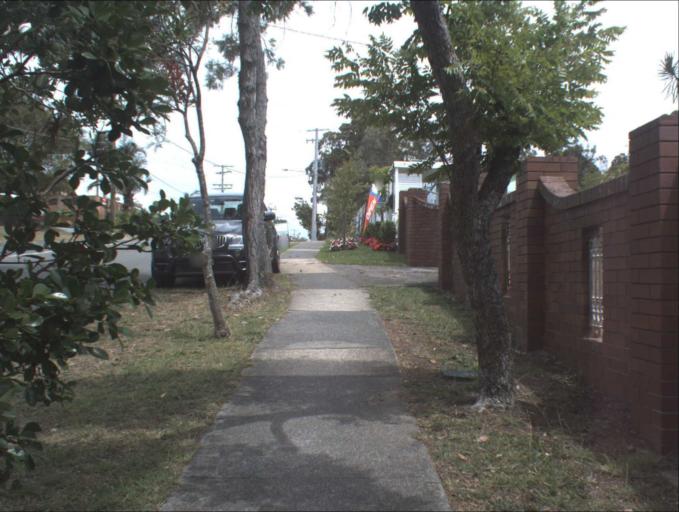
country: AU
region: Queensland
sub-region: Logan
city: Springwood
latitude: -27.6281
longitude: 153.1346
